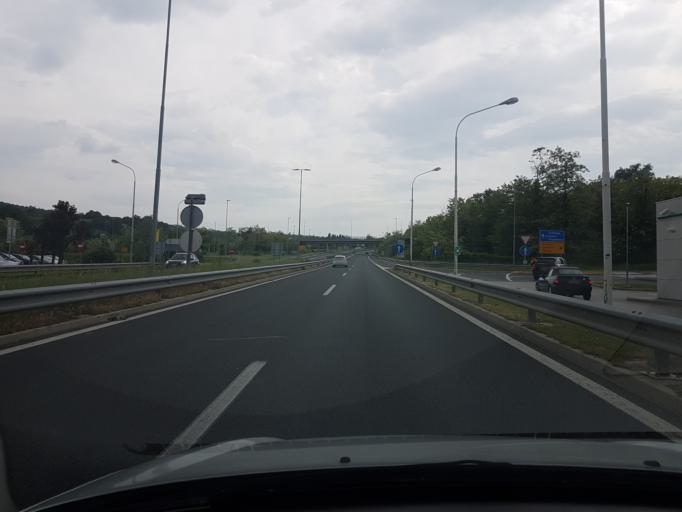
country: SI
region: Koper-Capodistria
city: Spodnje Skofije
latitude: 45.5798
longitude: 13.7966
